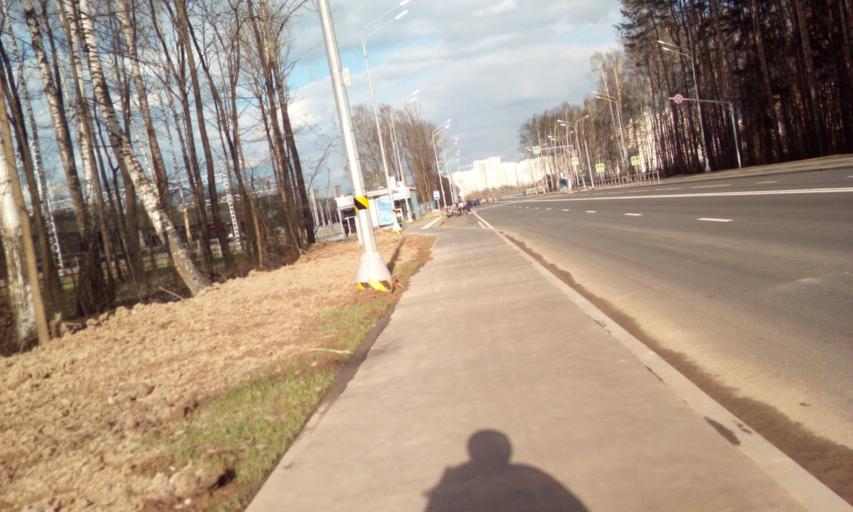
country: RU
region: Moscow
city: Novo-Peredelkino
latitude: 55.6456
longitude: 37.3139
